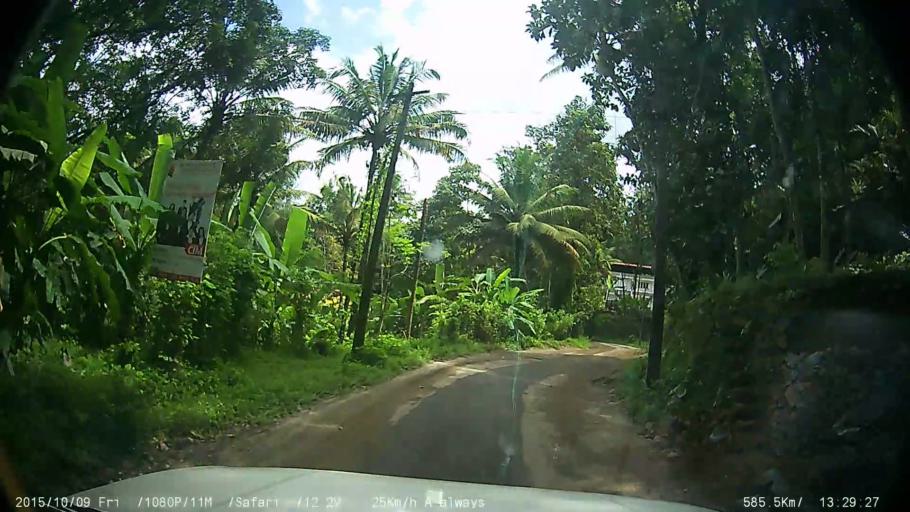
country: IN
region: Kerala
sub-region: Ernakulam
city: Ramamangalam
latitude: 9.9179
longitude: 76.5528
